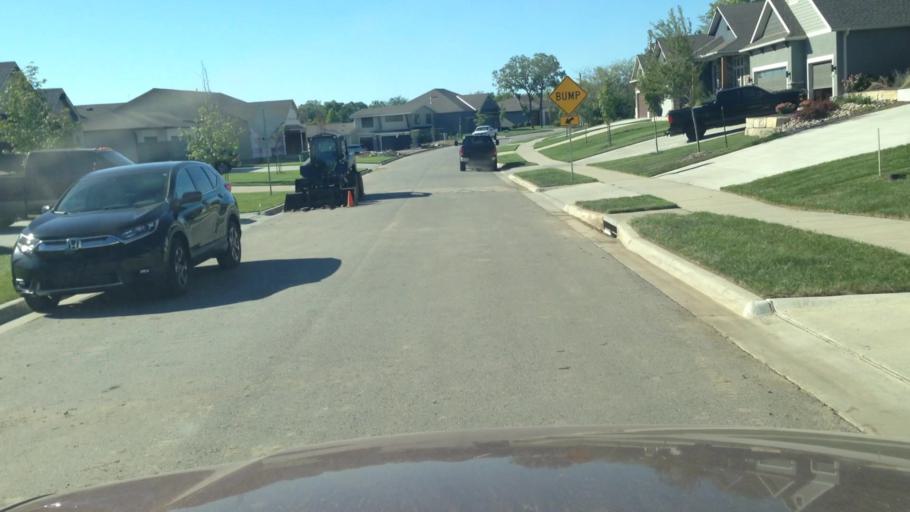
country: US
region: Kansas
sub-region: Douglas County
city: Lawrence
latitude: 38.9595
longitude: -95.3199
